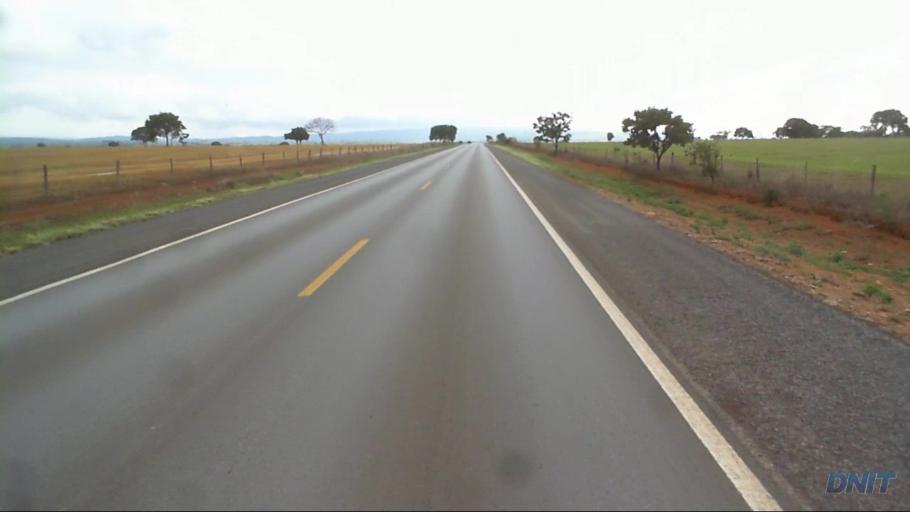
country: BR
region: Goias
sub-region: Padre Bernardo
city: Padre Bernardo
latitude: -15.2174
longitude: -48.6132
